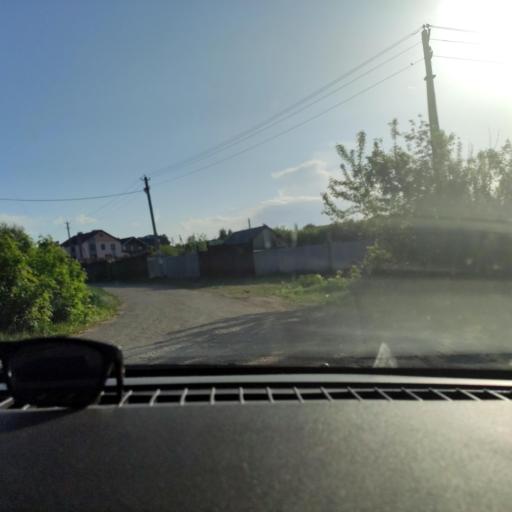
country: RU
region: Samara
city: Volzhskiy
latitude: 53.4391
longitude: 50.1716
